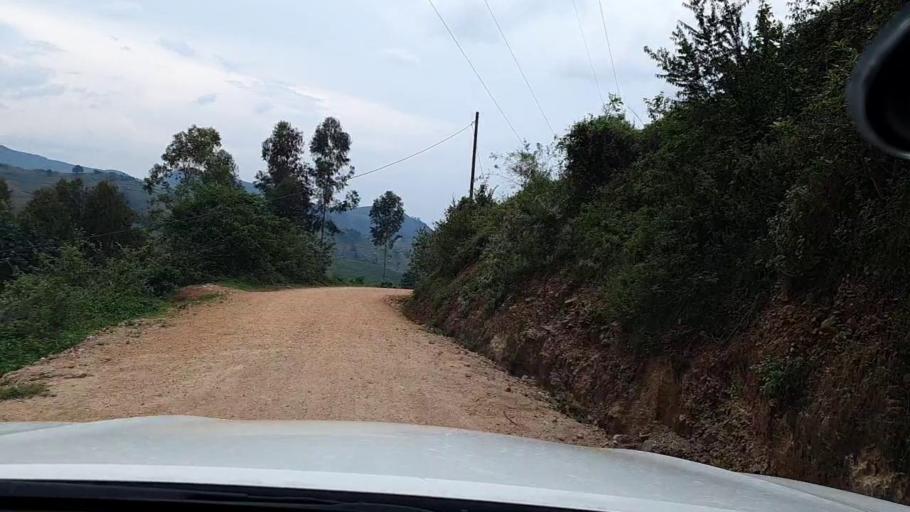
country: RW
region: Western Province
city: Kibuye
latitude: -2.2828
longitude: 29.3023
